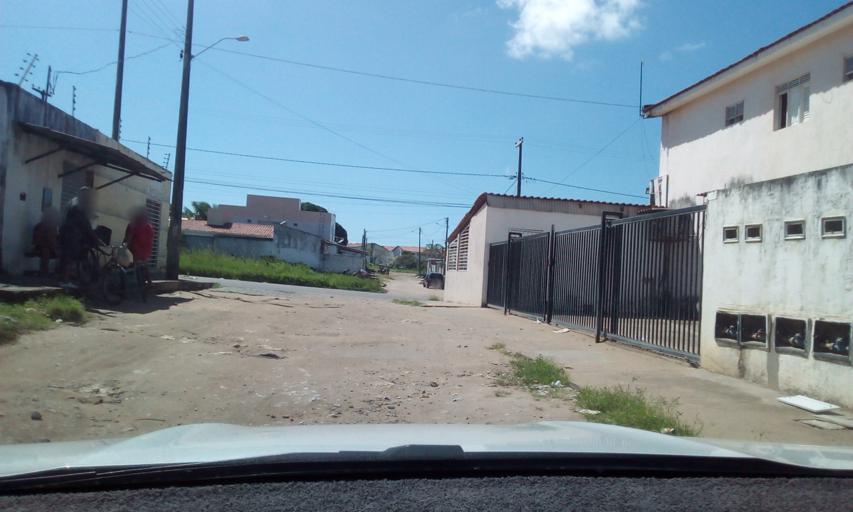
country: BR
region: Paraiba
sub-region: Joao Pessoa
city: Joao Pessoa
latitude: -7.2017
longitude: -34.8335
